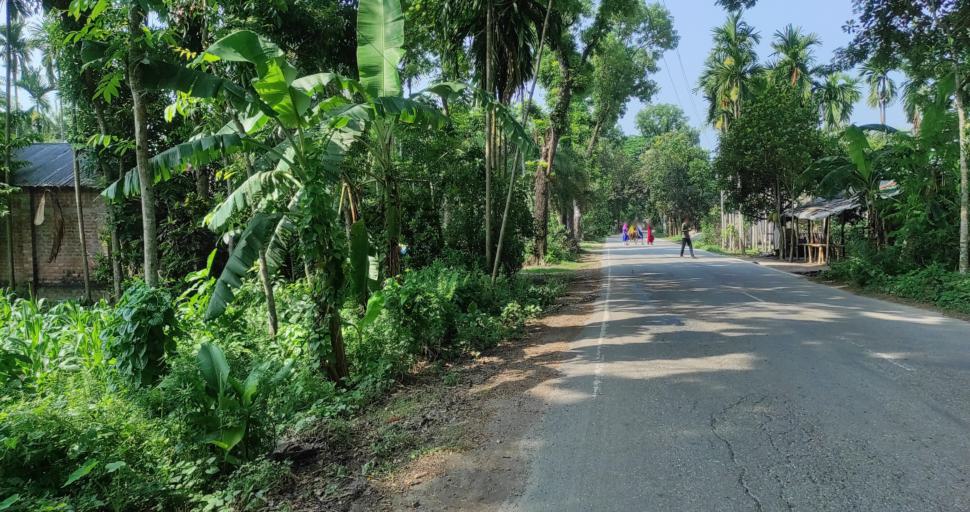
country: BD
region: Rajshahi
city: Ishurdi
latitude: 24.2597
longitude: 89.0489
